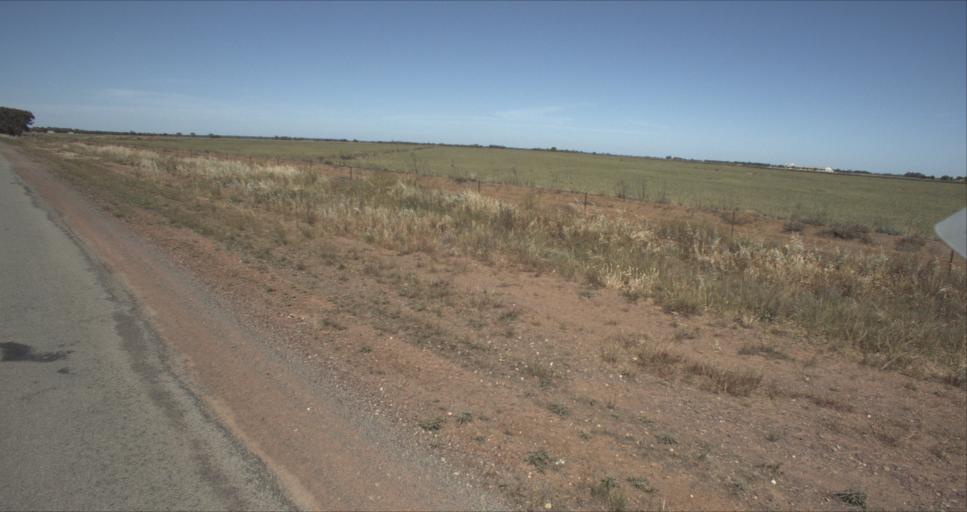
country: AU
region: New South Wales
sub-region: Leeton
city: Leeton
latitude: -34.5526
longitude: 146.3143
